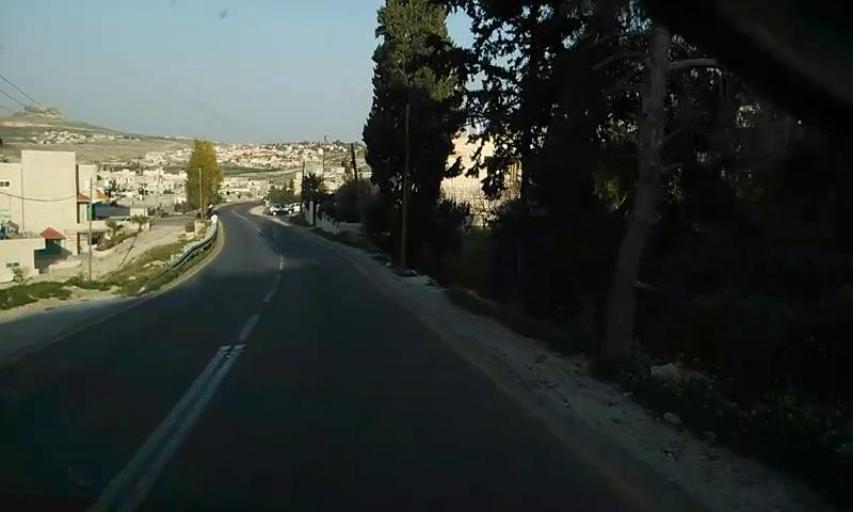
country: PS
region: West Bank
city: Jannatah
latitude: 31.6514
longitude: 35.2108
